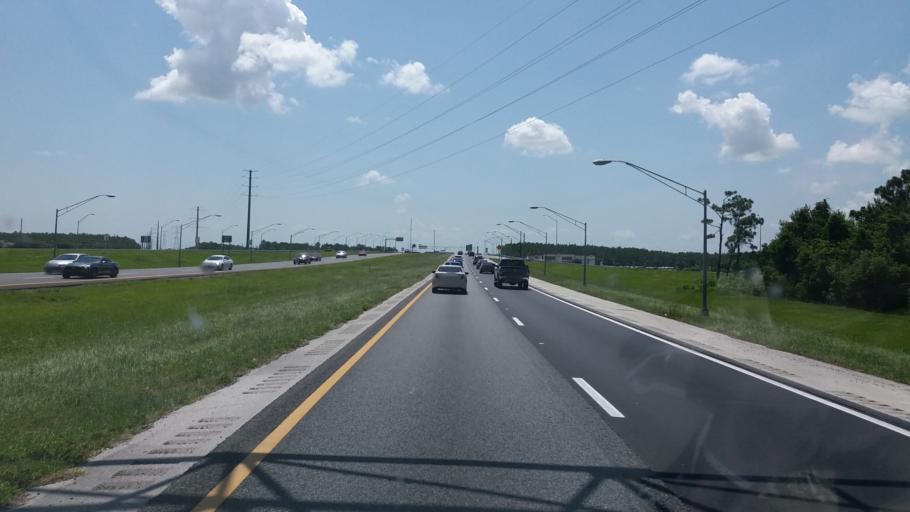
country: US
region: Florida
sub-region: Orange County
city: Hunters Creek
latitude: 28.3743
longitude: -81.4091
